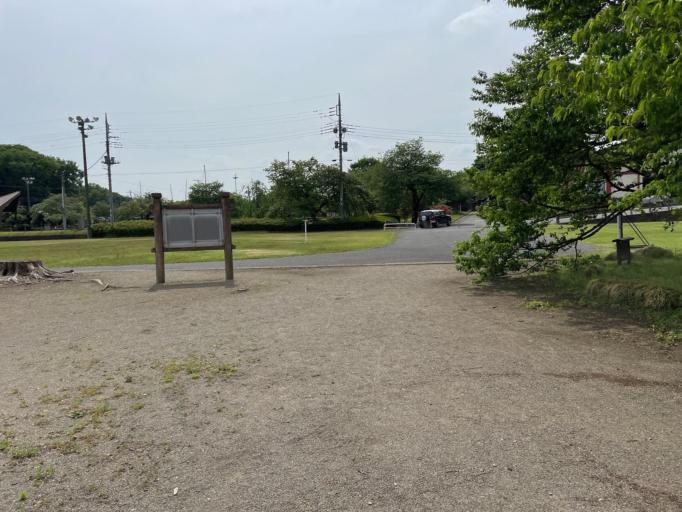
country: JP
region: Tochigi
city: Mibu
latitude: 36.3852
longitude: 139.8124
